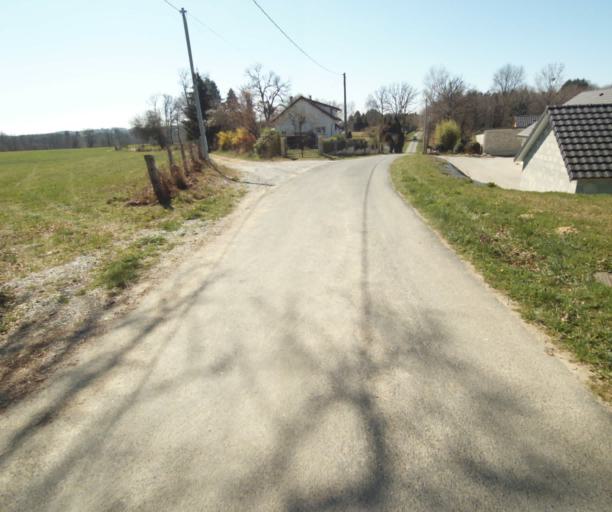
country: FR
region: Limousin
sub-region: Departement de la Correze
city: Saint-Mexant
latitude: 45.3124
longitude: 1.6576
